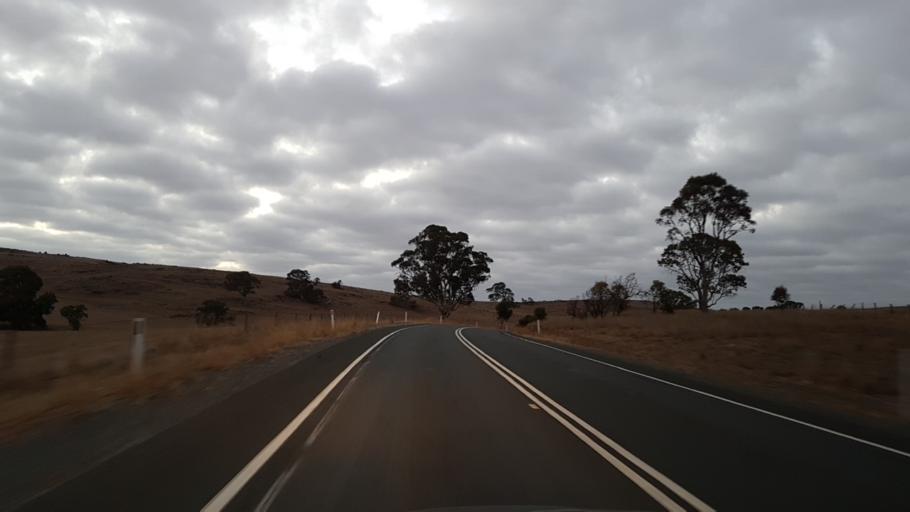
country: AU
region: South Australia
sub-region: Mount Barker
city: Nairne
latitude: -35.0359
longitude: 138.9850
